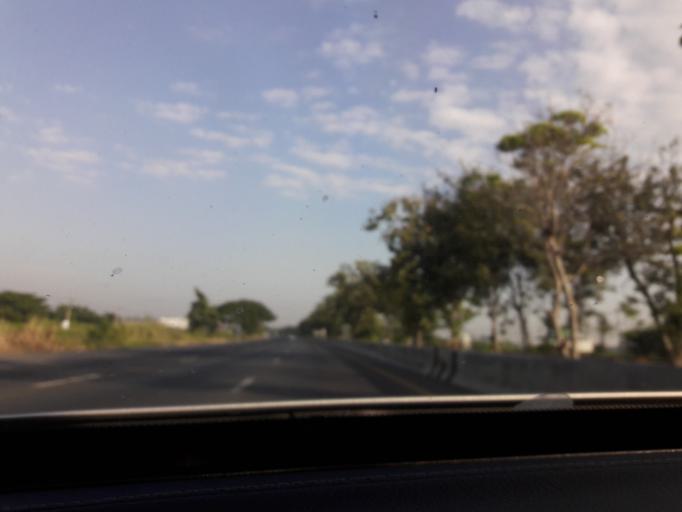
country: TH
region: Ang Thong
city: Chaiyo
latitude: 14.6483
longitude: 100.4745
